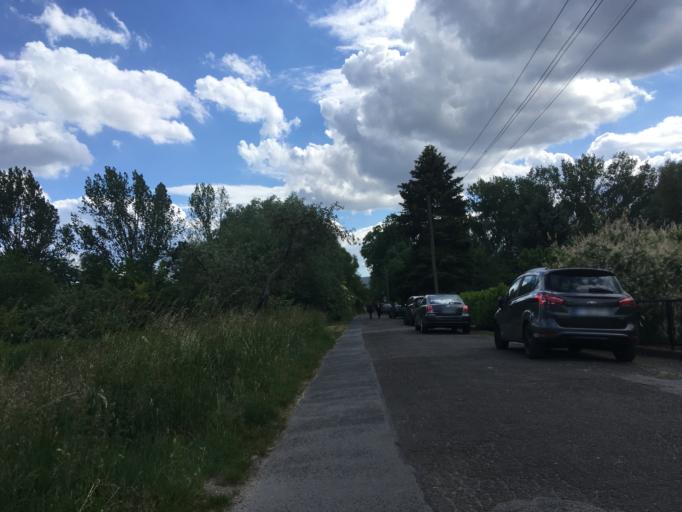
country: DE
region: Berlin
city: Wartenberg
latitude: 52.5741
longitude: 13.5311
